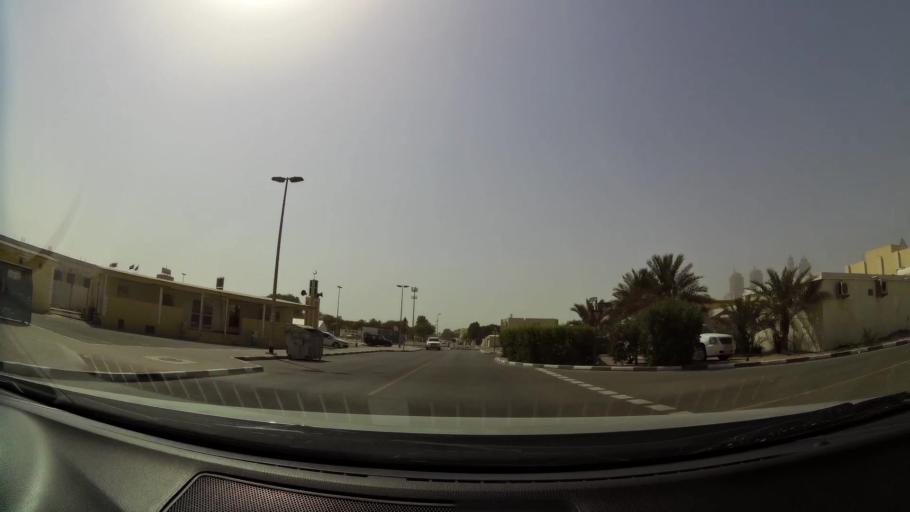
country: AE
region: Dubai
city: Dubai
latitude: 25.1678
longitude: 55.2587
